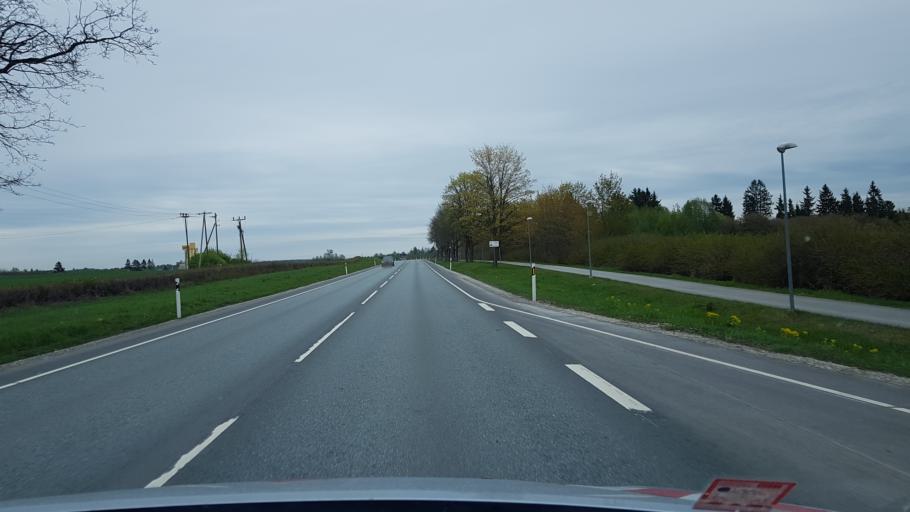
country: EE
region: Jaervamaa
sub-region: Paide linn
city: Paide
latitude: 58.9105
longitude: 25.5907
